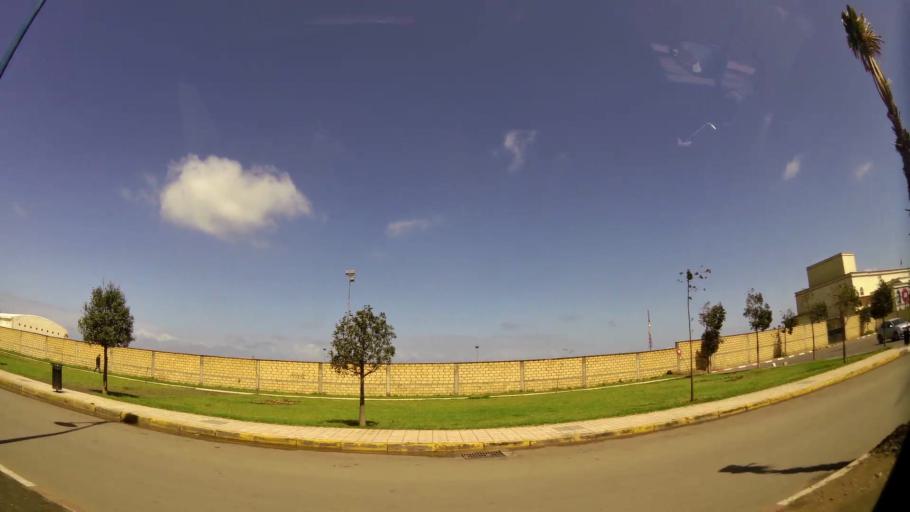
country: MA
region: Grand Casablanca
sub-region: Mediouna
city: Tit Mellil
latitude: 33.6340
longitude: -7.4564
